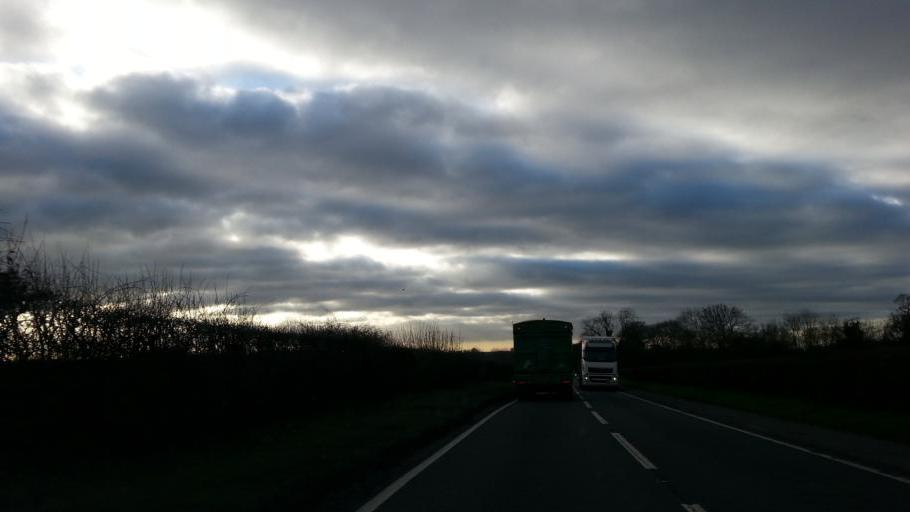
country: GB
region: England
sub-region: Suffolk
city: Great Barton
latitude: 52.2609
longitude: 0.7572
